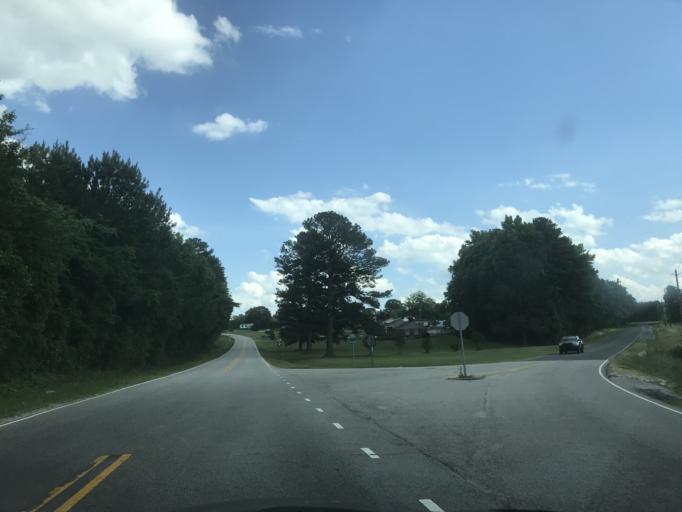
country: US
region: North Carolina
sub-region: Nash County
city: Spring Hope
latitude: 35.9369
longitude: -78.2074
